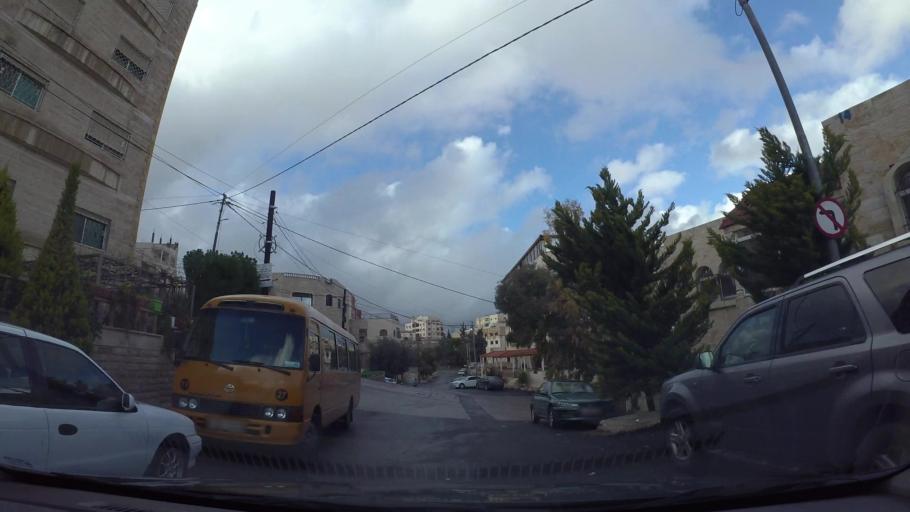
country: JO
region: Amman
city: Amman
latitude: 32.0022
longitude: 35.9217
